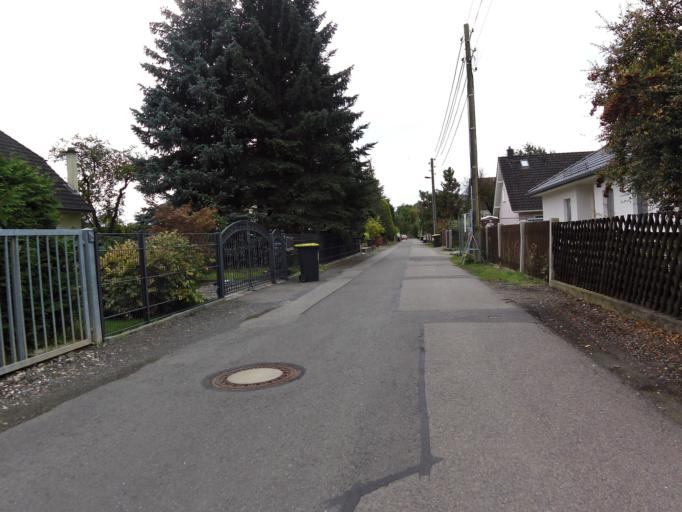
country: DE
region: Saxony
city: Grossposna
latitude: 51.3156
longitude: 12.4446
